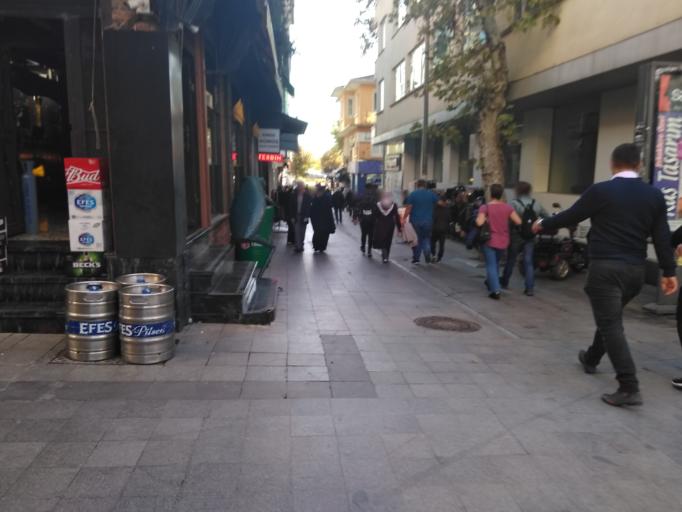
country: TR
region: Istanbul
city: Maltepe
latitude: 40.8888
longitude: 29.1887
